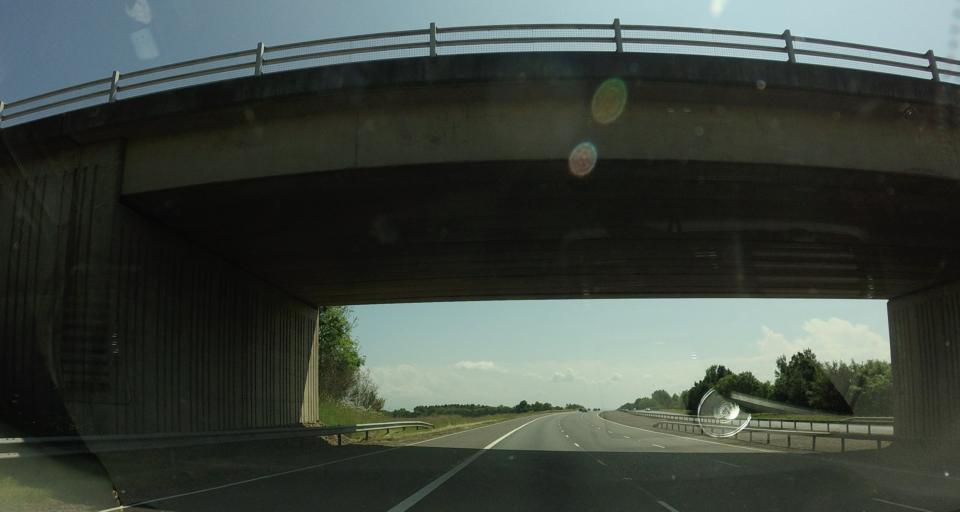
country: GB
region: Scotland
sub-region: Dumfries and Galloway
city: Gretna
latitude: 55.0251
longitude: -3.1280
